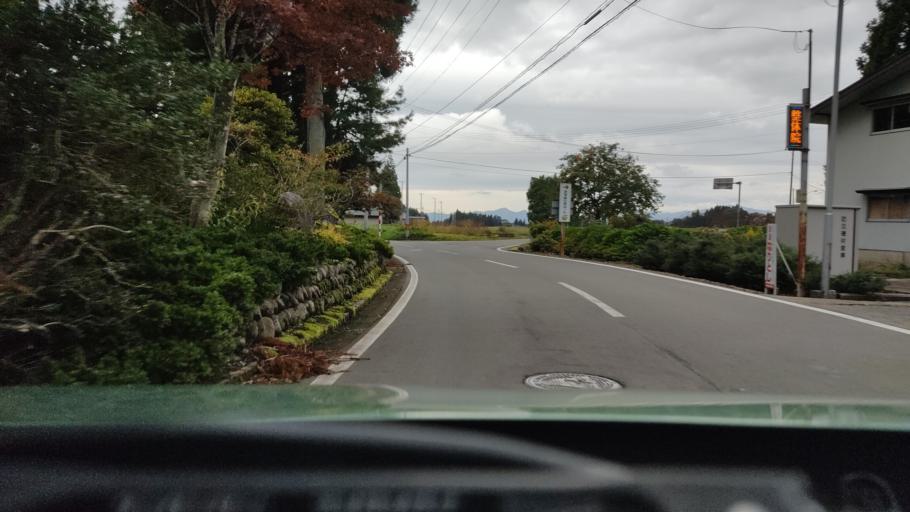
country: JP
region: Akita
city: Kakunodatemachi
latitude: 39.5109
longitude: 140.6495
